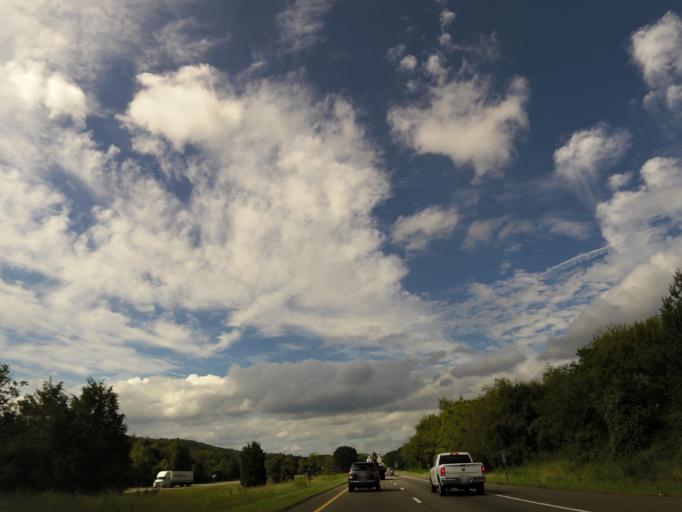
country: US
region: Tennessee
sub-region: Monroe County
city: Sweetwater
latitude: 35.6863
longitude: -84.4367
